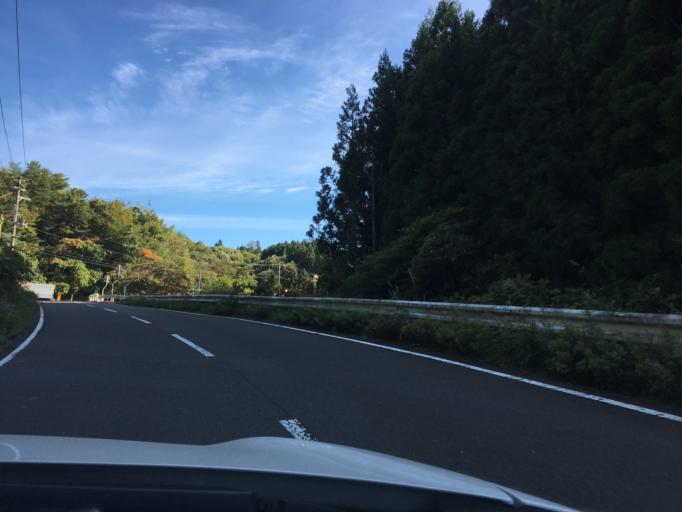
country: JP
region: Fukushima
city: Ishikawa
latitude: 37.2047
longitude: 140.5858
